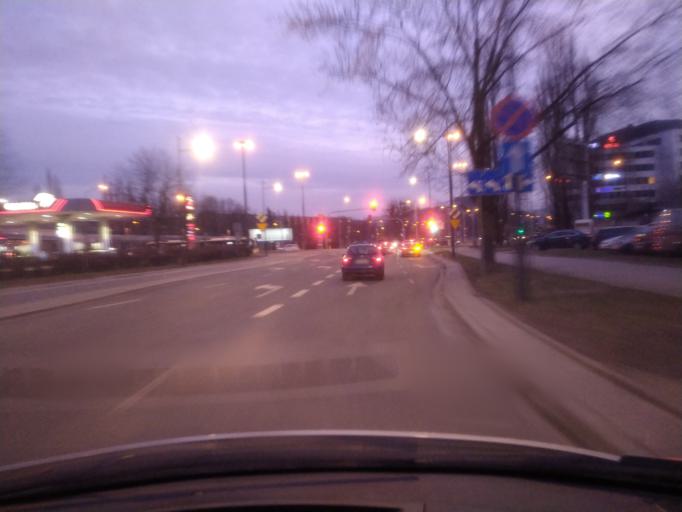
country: PL
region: Masovian Voivodeship
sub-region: Warszawa
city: Praga Poludnie
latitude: 52.2370
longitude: 21.0868
